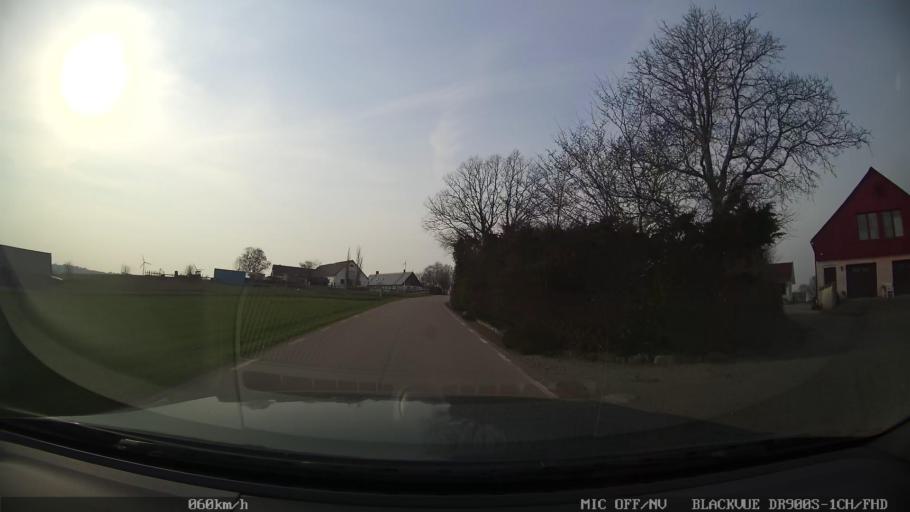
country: SE
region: Skane
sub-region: Ystads Kommun
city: Ystad
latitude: 55.4664
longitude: 13.8143
